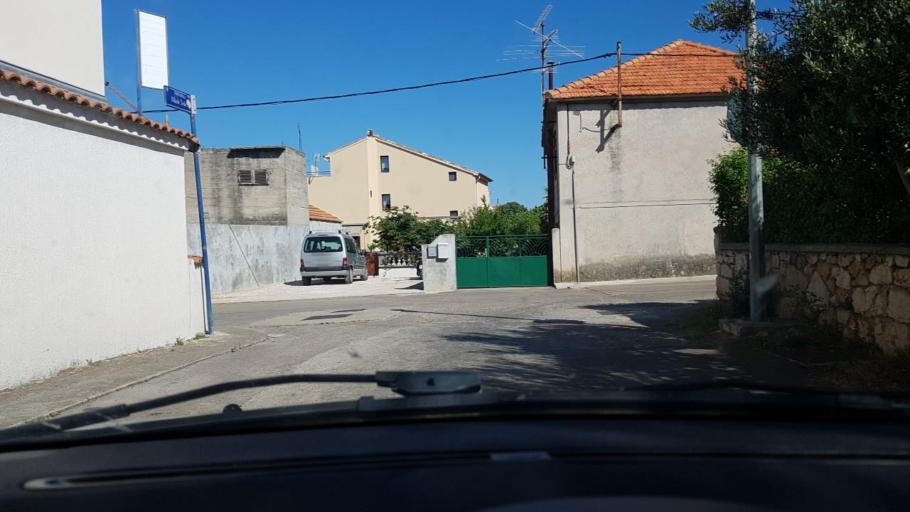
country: HR
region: Sibensko-Kniniska
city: Vodice
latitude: 43.7601
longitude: 15.7800
